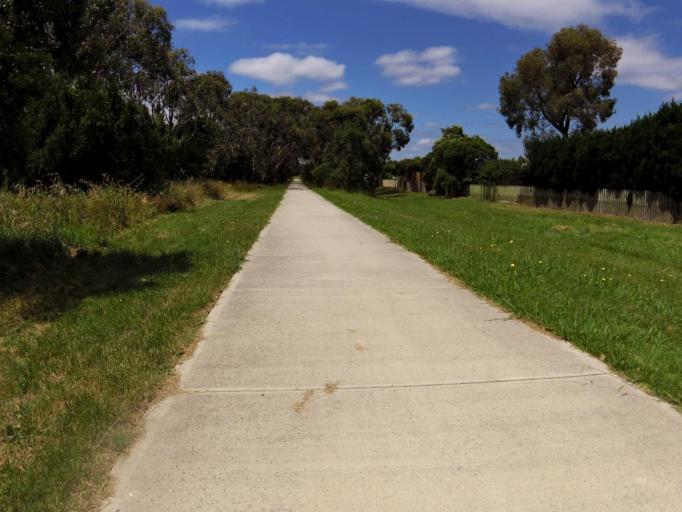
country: AU
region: Victoria
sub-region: Casey
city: Endeavour Hills
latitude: -37.9670
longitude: 145.2567
